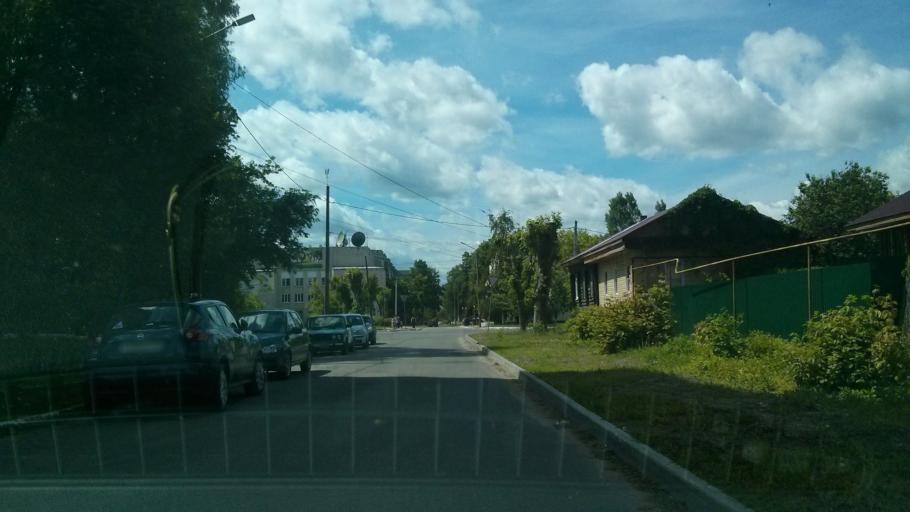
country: RU
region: Vladimir
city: Murom
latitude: 55.5694
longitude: 42.0607
